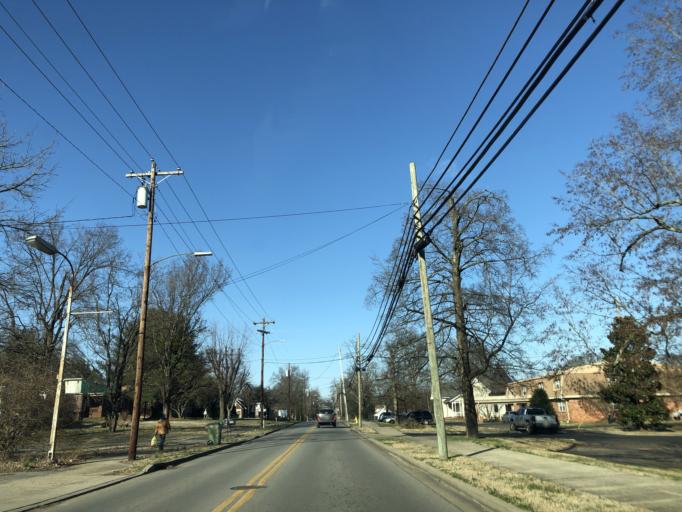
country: US
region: Tennessee
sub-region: Sumner County
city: Gallatin
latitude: 36.3961
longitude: -86.4465
